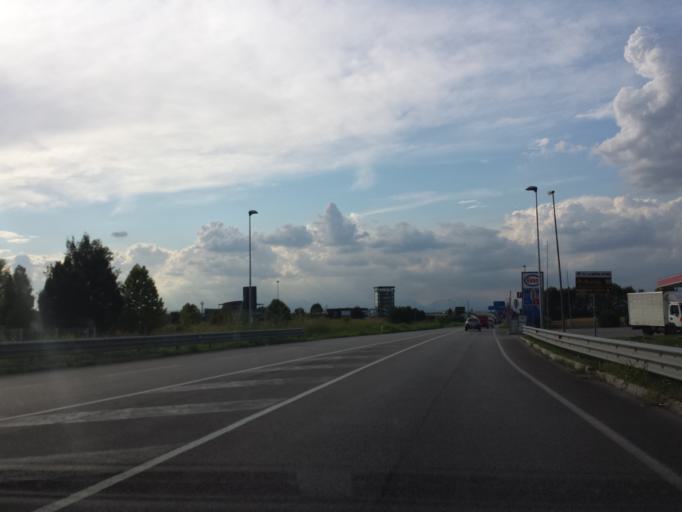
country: IT
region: Veneto
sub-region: Provincia di Vicenza
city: Torri di Quartesolo
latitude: 45.5094
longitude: 11.6315
